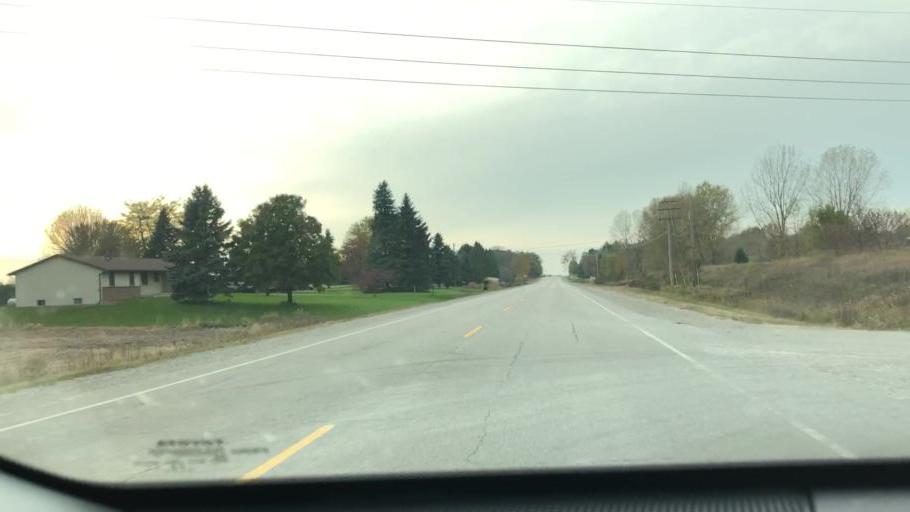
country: US
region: Wisconsin
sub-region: Outagamie County
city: Seymour
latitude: 44.5010
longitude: -88.3560
